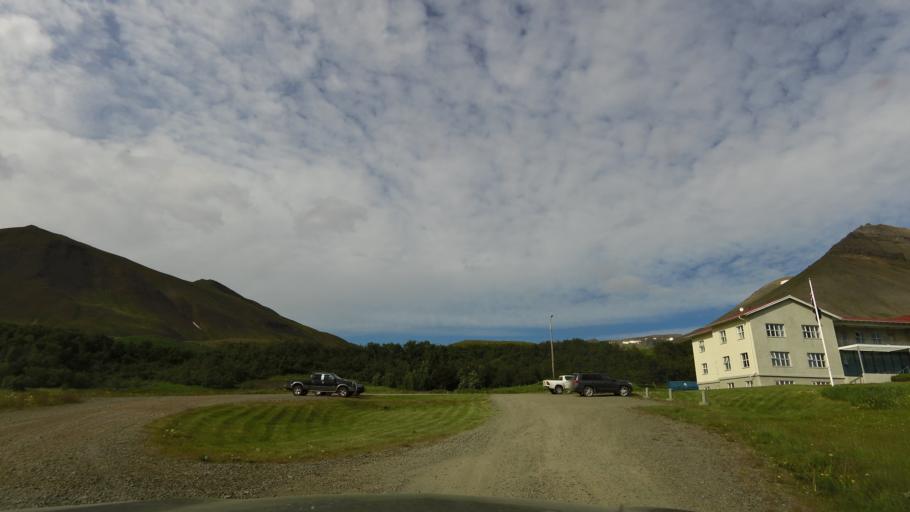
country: IS
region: Westfjords
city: Isafjoerdur
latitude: 65.7594
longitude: -23.4522
